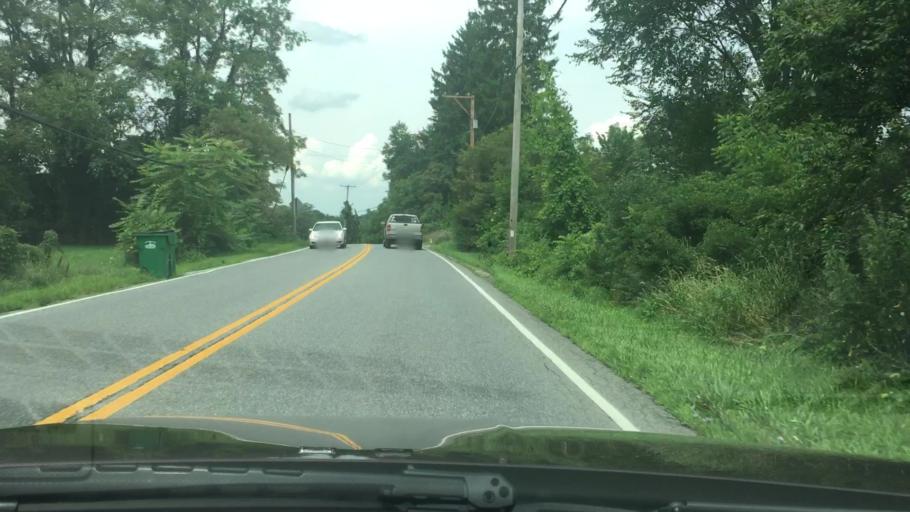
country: US
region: New York
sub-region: Dutchess County
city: Hillside Lake
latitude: 41.6498
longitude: -73.8269
